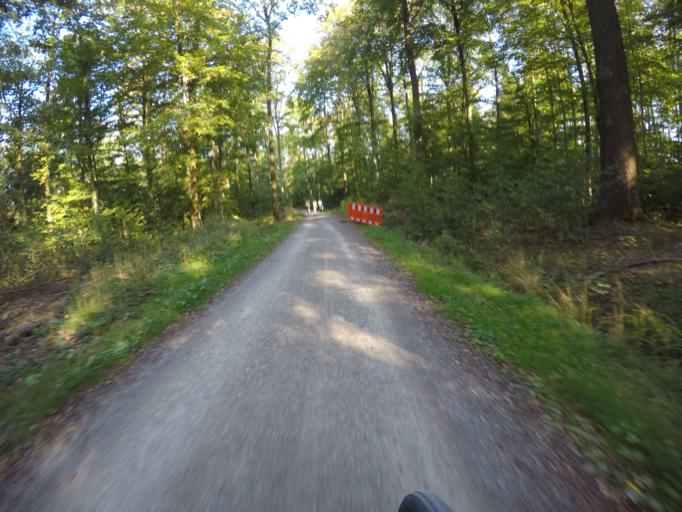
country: DE
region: Baden-Wuerttemberg
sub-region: Regierungsbezirk Stuttgart
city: Stuttgart
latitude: 48.7544
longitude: 9.1184
